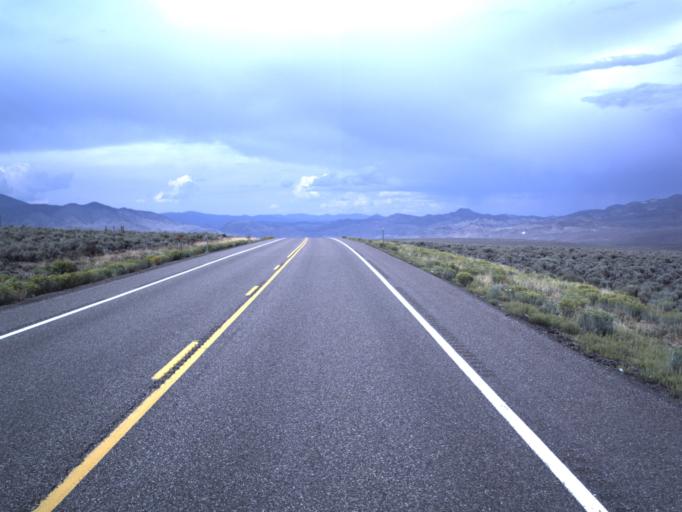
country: US
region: Utah
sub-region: Piute County
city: Junction
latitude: 38.3385
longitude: -112.2176
